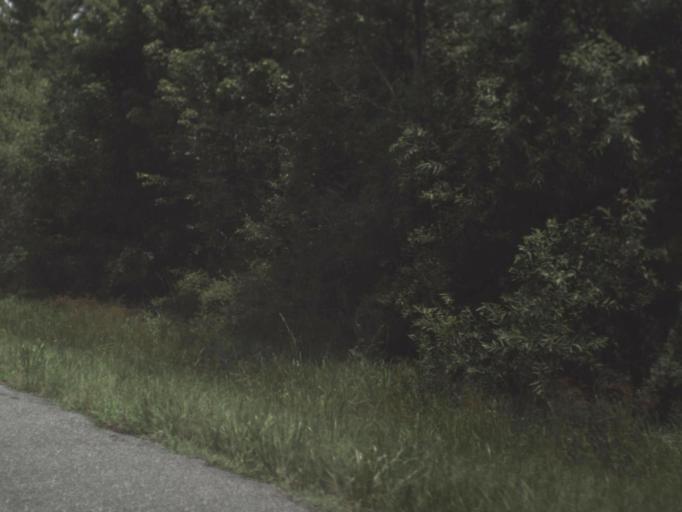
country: US
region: Florida
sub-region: Lafayette County
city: Mayo
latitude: 29.8854
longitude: -83.3030
